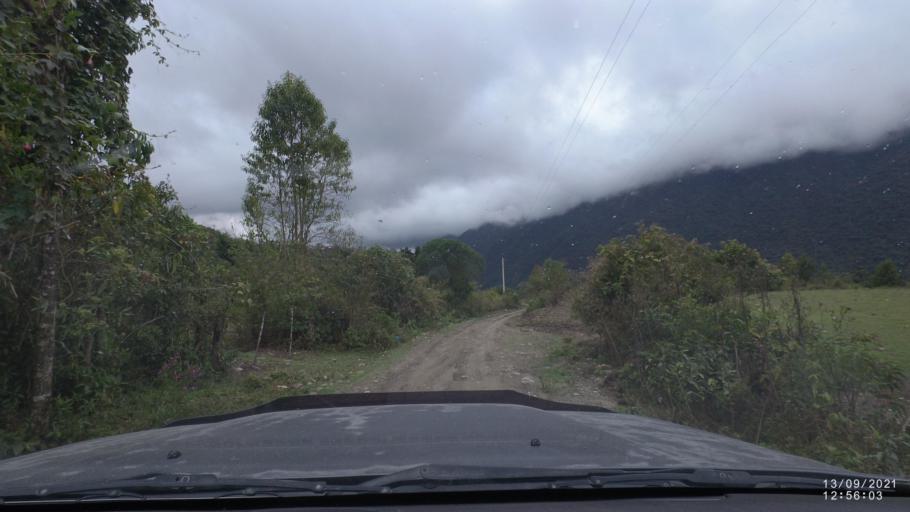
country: BO
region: Cochabamba
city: Colomi
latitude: -17.2404
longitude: -65.8207
